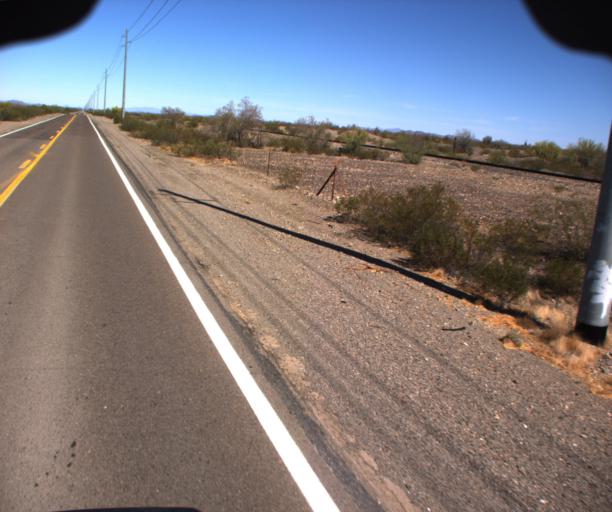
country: US
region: Arizona
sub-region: La Paz County
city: Salome
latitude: 33.7796
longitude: -113.8052
